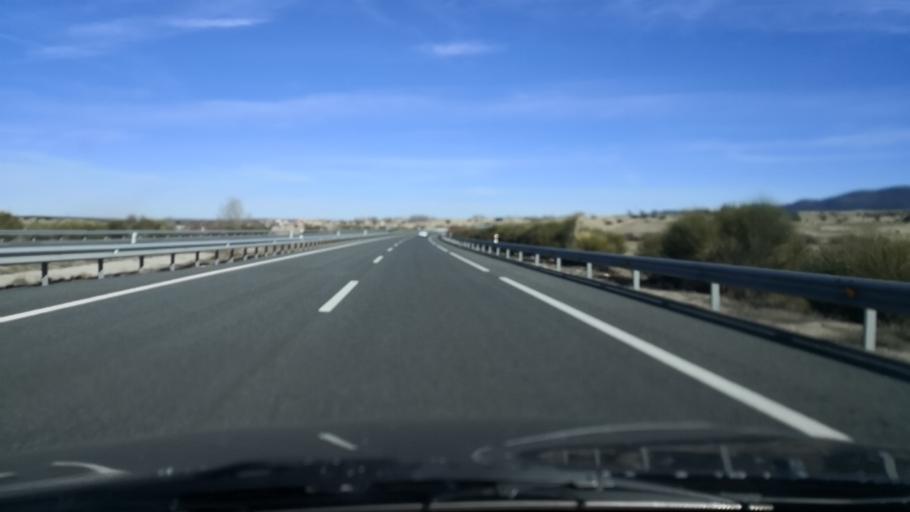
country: ES
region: Castille and Leon
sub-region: Provincia de Avila
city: Berrocalejo de Aragona
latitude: 40.6809
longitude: -4.6026
